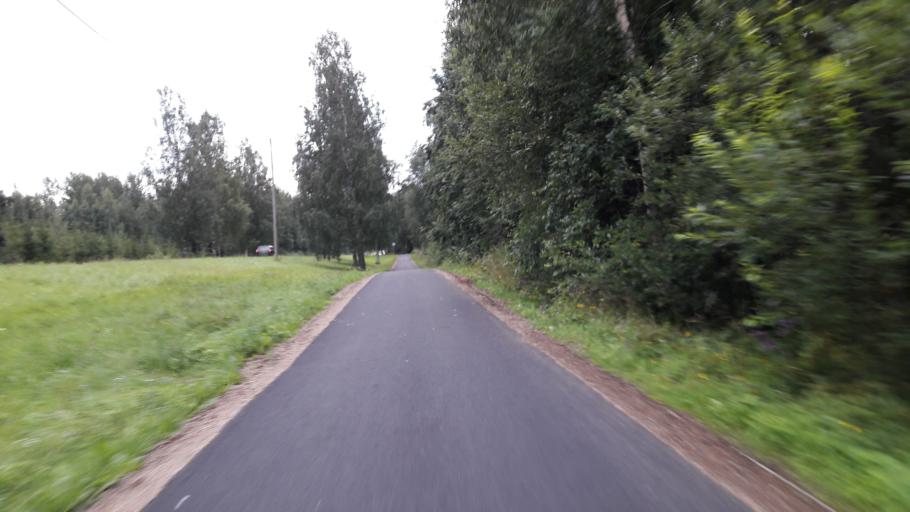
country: FI
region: North Karelia
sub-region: Joensuu
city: Joensuu
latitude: 62.5361
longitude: 29.8474
